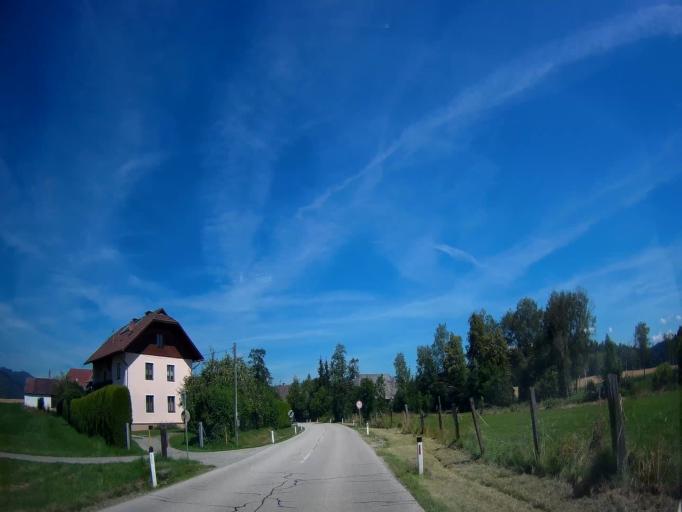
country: AT
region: Carinthia
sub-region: Politischer Bezirk Sankt Veit an der Glan
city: St. Georgen am Laengsee
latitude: 46.7997
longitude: 14.4135
